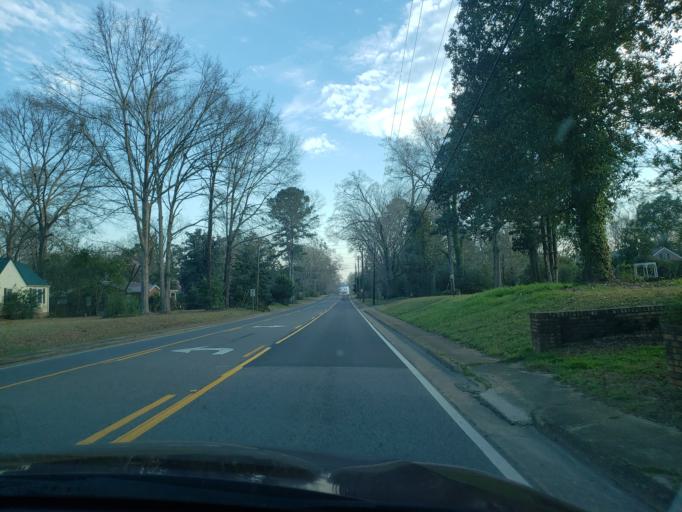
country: US
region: Alabama
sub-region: Hale County
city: Greensboro
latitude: 32.7119
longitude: -87.5959
